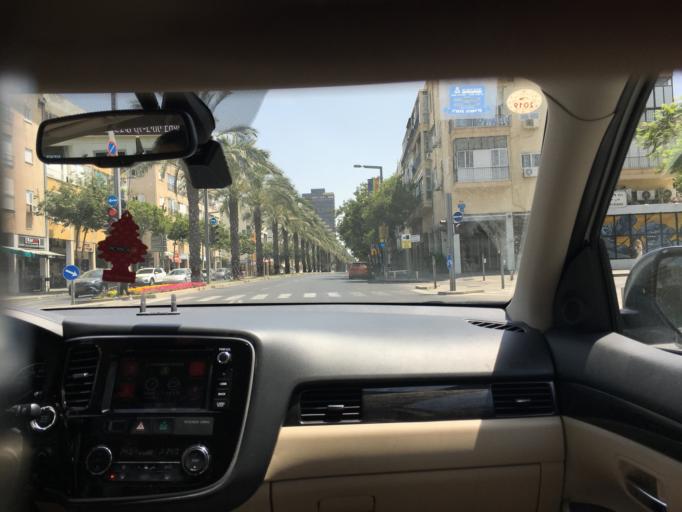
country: IL
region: Tel Aviv
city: Tel Aviv
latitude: 32.0911
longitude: 34.7828
